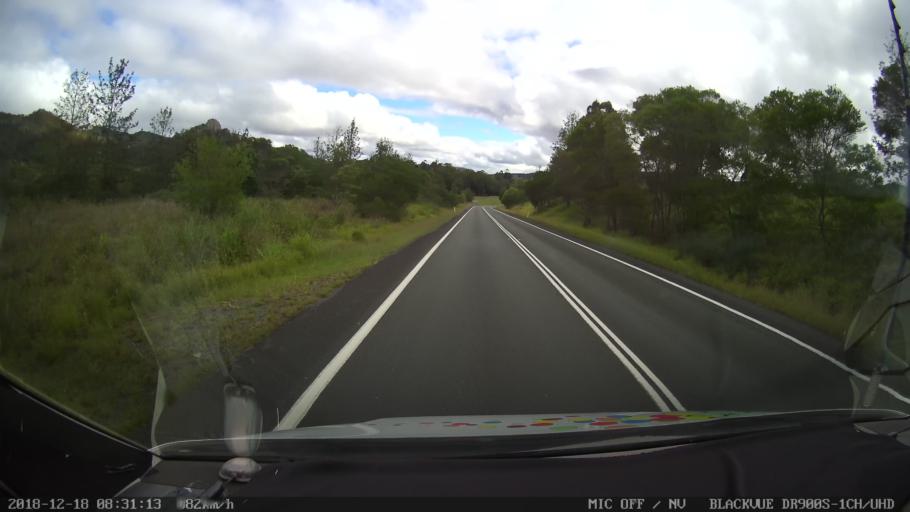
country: AU
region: New South Wales
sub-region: Kyogle
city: Kyogle
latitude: -28.3154
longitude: 152.7762
